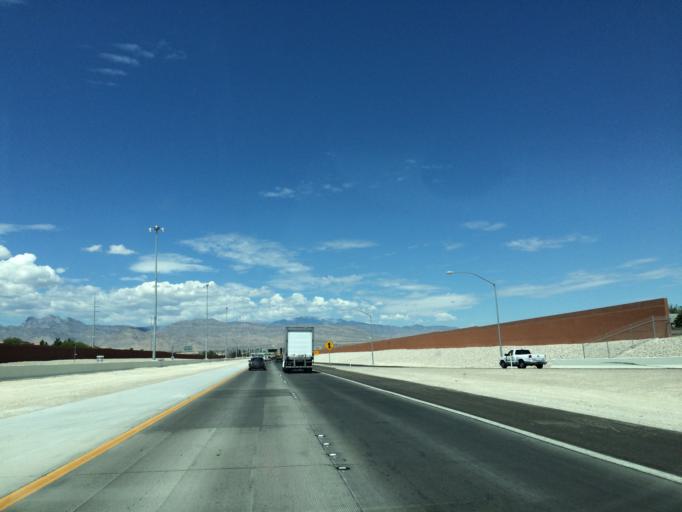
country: US
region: Nevada
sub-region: Clark County
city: North Las Vegas
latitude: 36.2754
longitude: -115.2284
